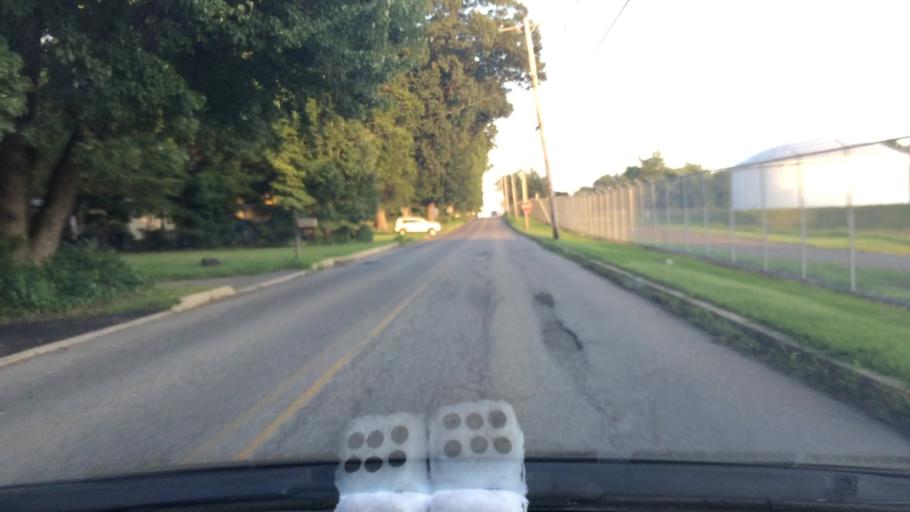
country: US
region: Pennsylvania
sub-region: Delaware County
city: Village Green-Green Ridge
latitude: 39.8619
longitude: -75.4492
